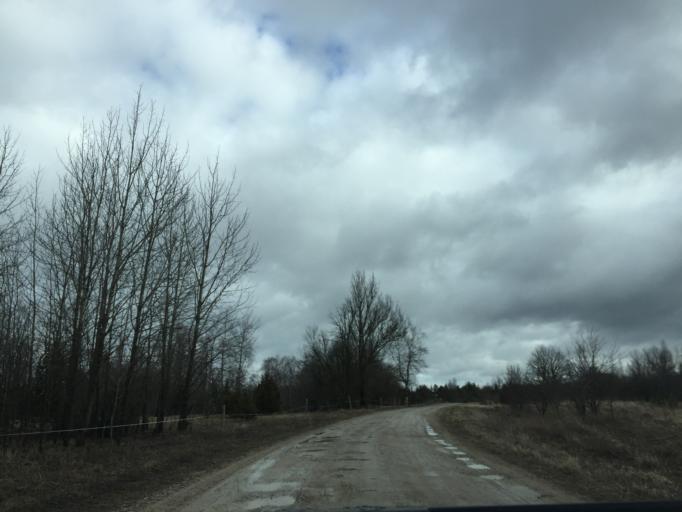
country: EE
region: Laeaene
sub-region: Haapsalu linn
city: Haapsalu
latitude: 58.6841
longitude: 23.5422
